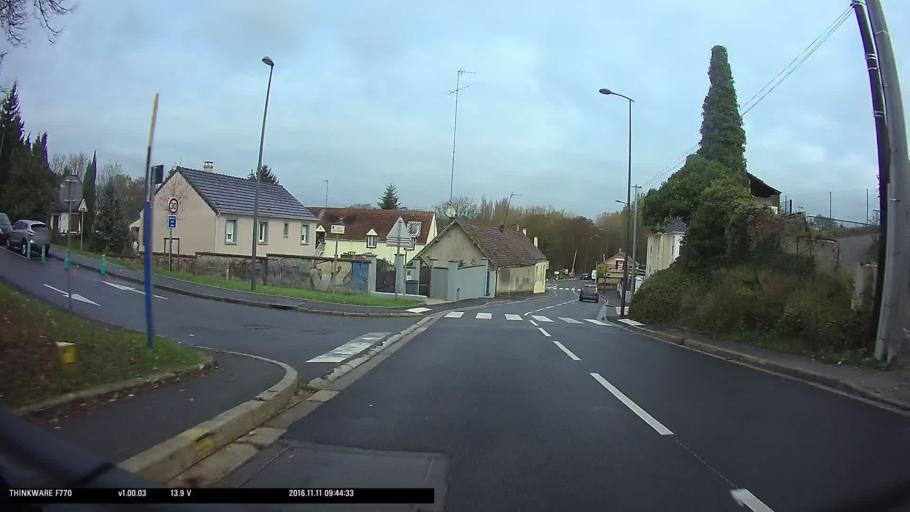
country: FR
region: Ile-de-France
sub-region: Departement du Val-d'Oise
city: Osny
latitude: 49.0635
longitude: 2.0507
